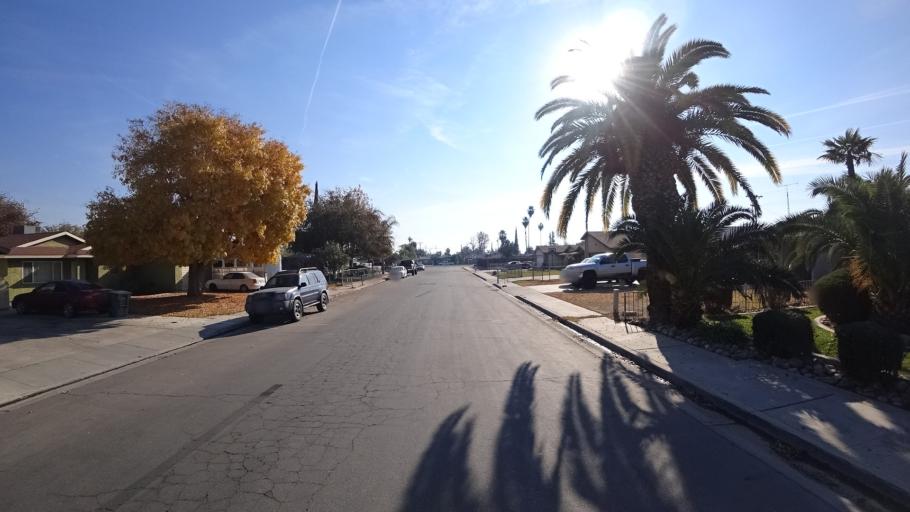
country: US
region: California
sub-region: Kern County
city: Greenfield
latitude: 35.3187
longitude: -119.0090
